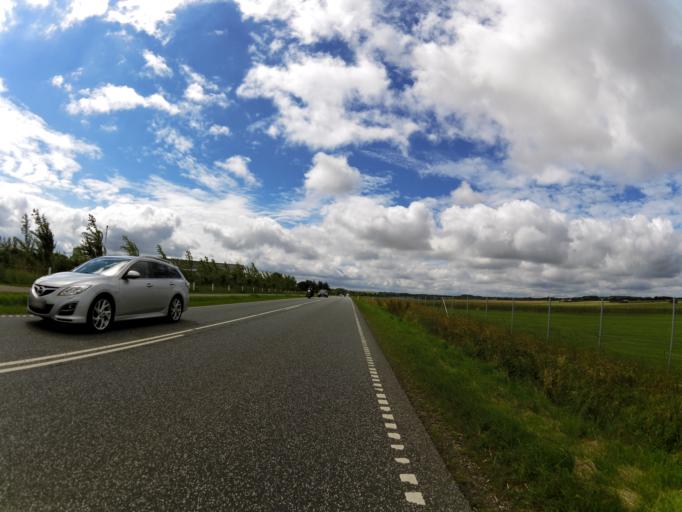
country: DK
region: Central Jutland
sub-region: Randers Kommune
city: Spentrup
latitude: 56.5944
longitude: 10.1340
